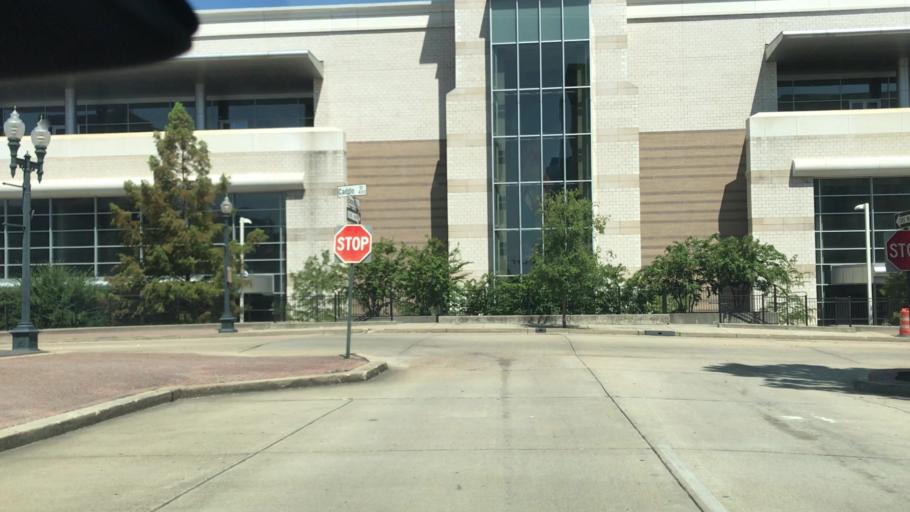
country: US
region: Louisiana
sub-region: Caddo Parish
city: Shreveport
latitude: 32.5158
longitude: -93.7510
